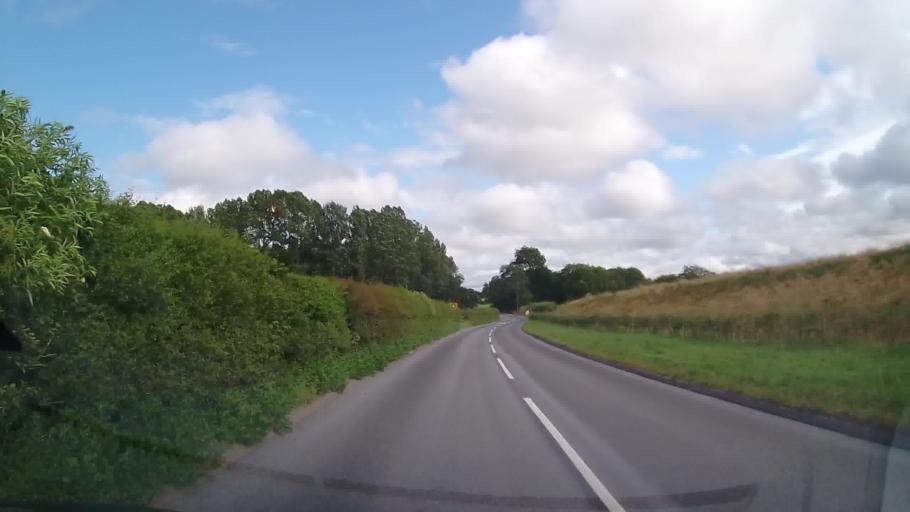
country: GB
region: England
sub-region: Shropshire
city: Pant
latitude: 52.8031
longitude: -3.0219
